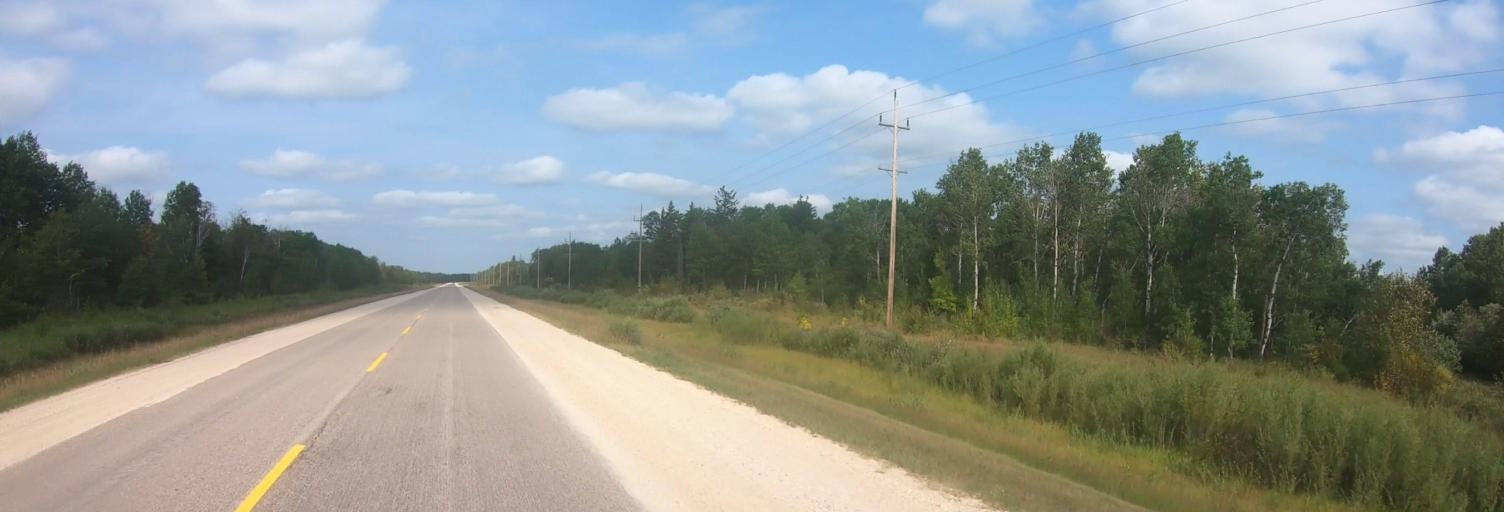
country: CA
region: Manitoba
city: La Broquerie
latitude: 49.2309
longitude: -96.3297
